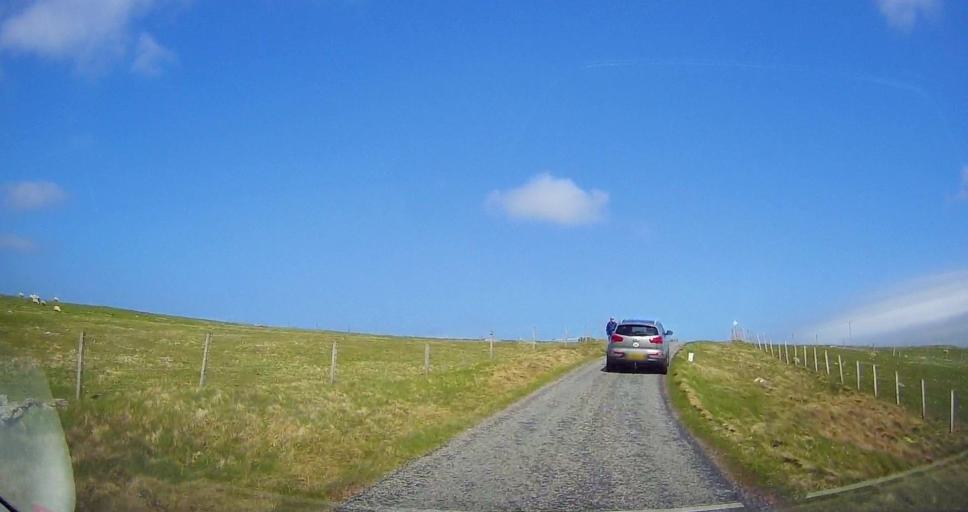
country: GB
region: Scotland
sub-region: Shetland Islands
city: Sandwick
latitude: 60.0726
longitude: -1.3407
